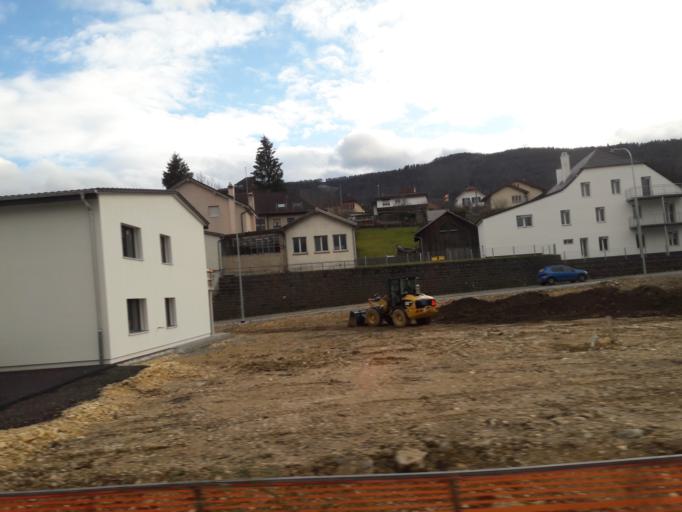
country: CH
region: Jura
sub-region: Delemont District
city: Courfaivre
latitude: 47.3350
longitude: 7.2874
